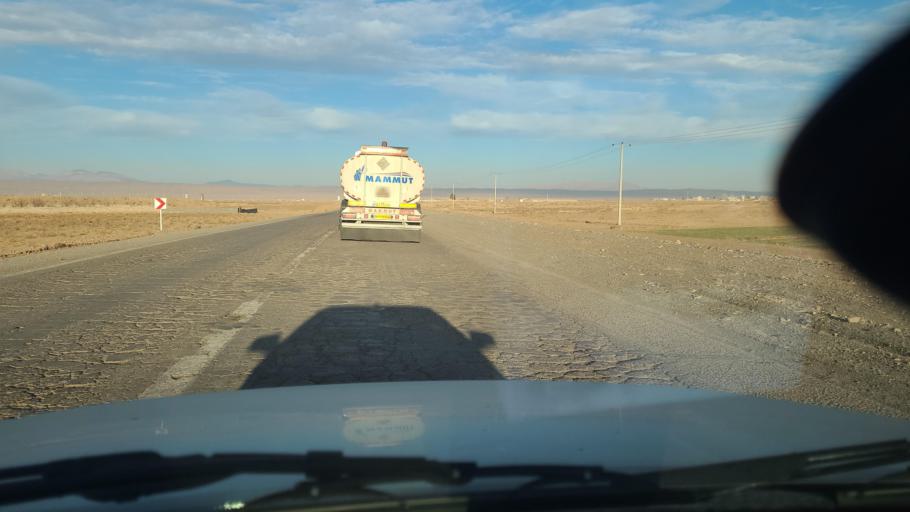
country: IR
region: Razavi Khorasan
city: Neqab
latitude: 36.6142
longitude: 57.5969
